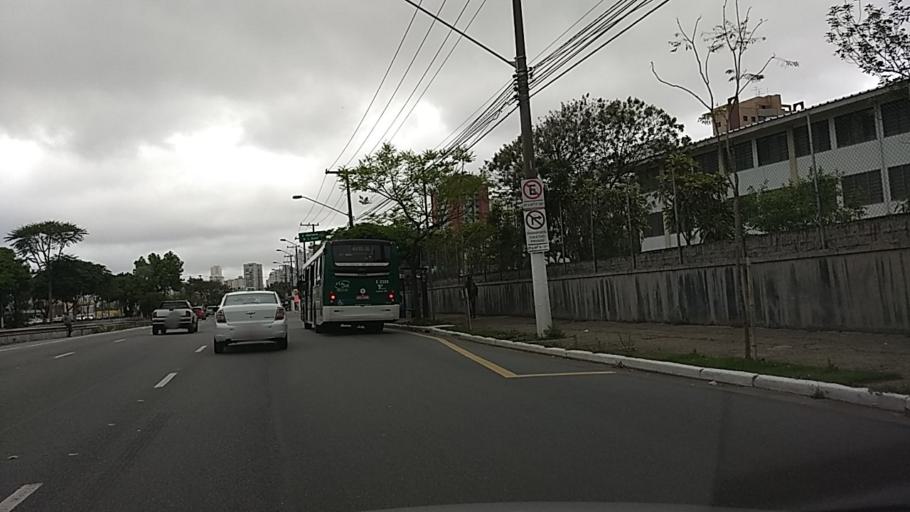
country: BR
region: Sao Paulo
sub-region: Sao Paulo
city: Sao Paulo
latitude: -23.6025
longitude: -46.6253
